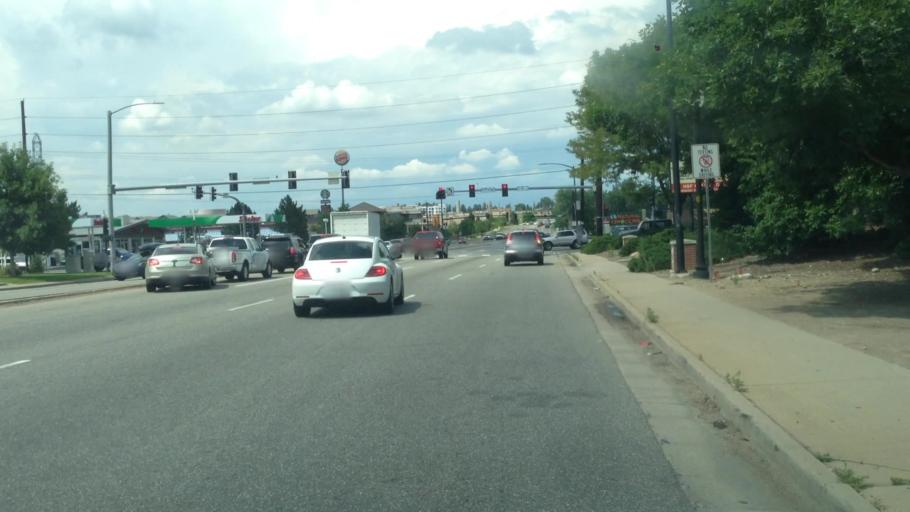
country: US
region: Colorado
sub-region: Jefferson County
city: Arvada
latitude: 39.7848
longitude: -105.1095
